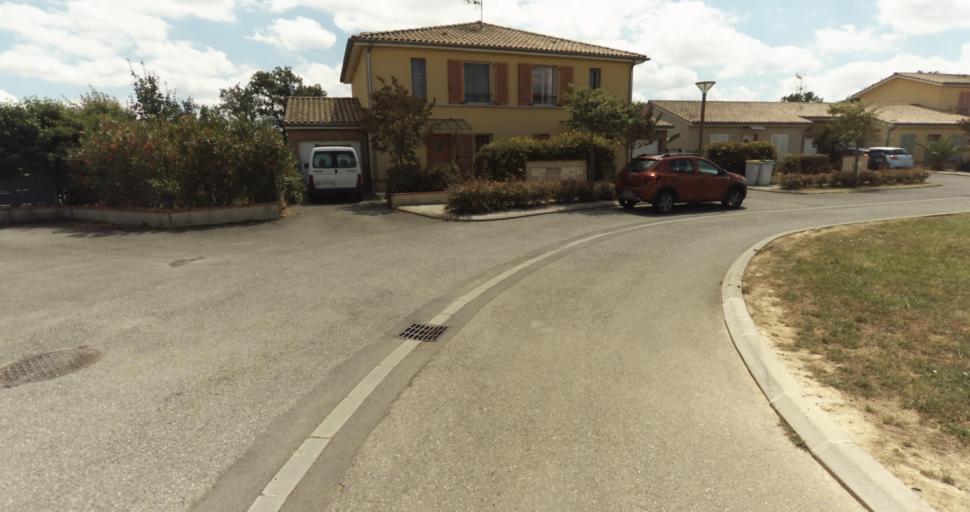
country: FR
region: Midi-Pyrenees
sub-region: Departement de la Haute-Garonne
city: Fontenilles
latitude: 43.5536
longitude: 1.1701
